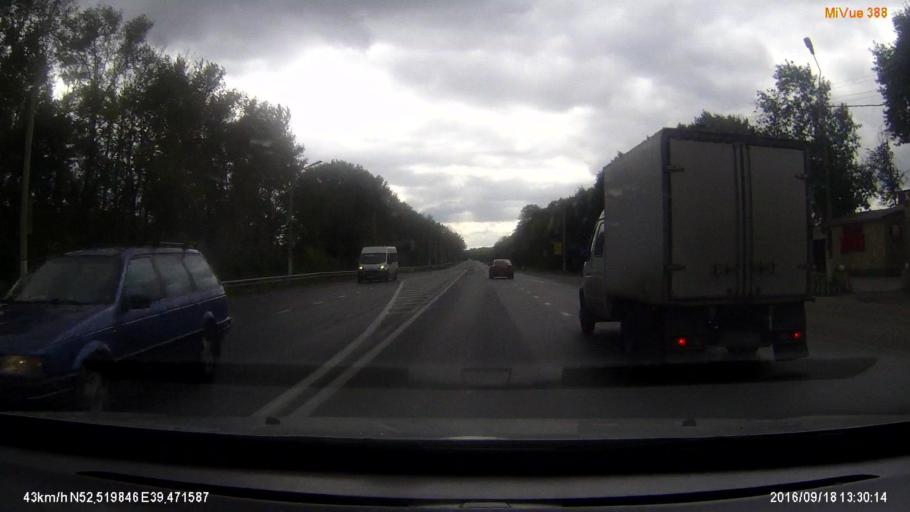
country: RU
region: Lipetsk
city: Borinskoye
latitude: 52.4709
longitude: 39.4205
